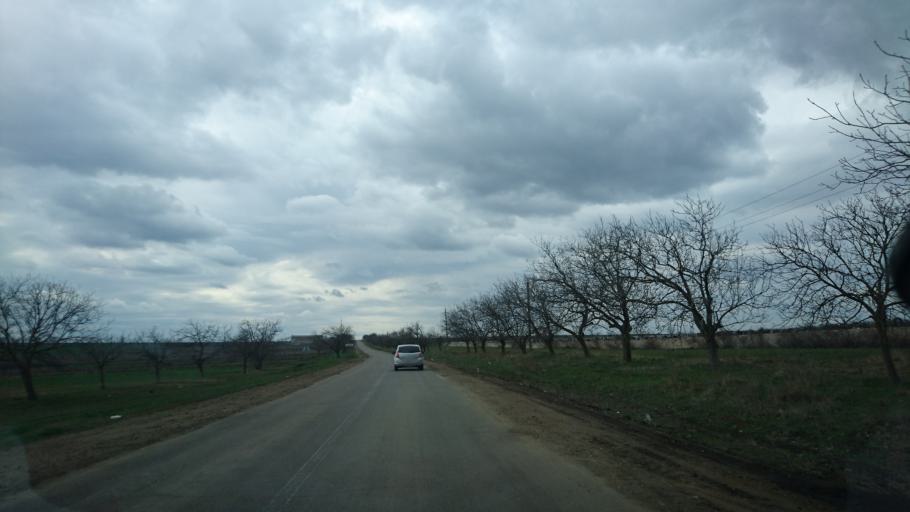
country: MD
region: Gagauzia
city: Comrat
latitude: 46.3066
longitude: 28.6207
